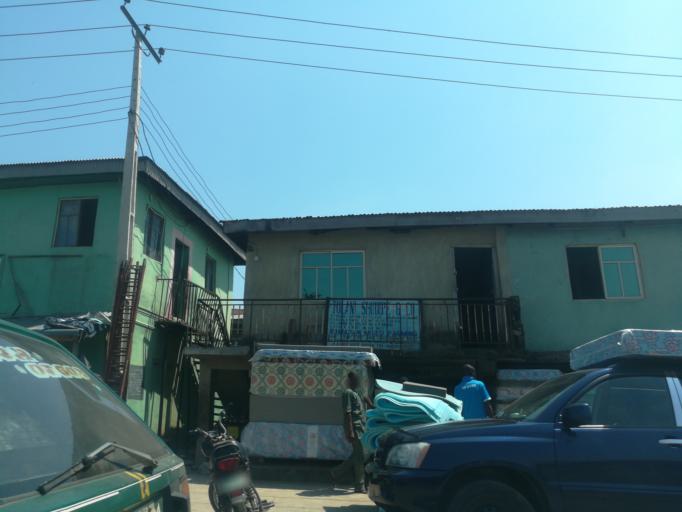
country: NG
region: Ogun
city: Abeokuta
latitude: 7.1555
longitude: 3.3479
